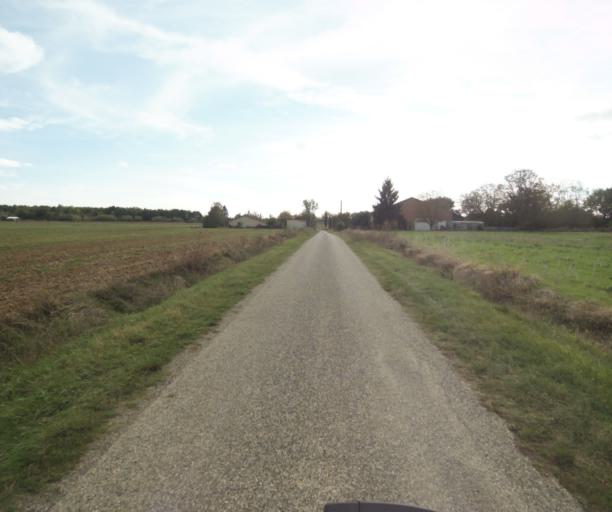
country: FR
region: Midi-Pyrenees
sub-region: Departement du Tarn-et-Garonne
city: Saint-Porquier
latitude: 43.9508
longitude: 1.1512
